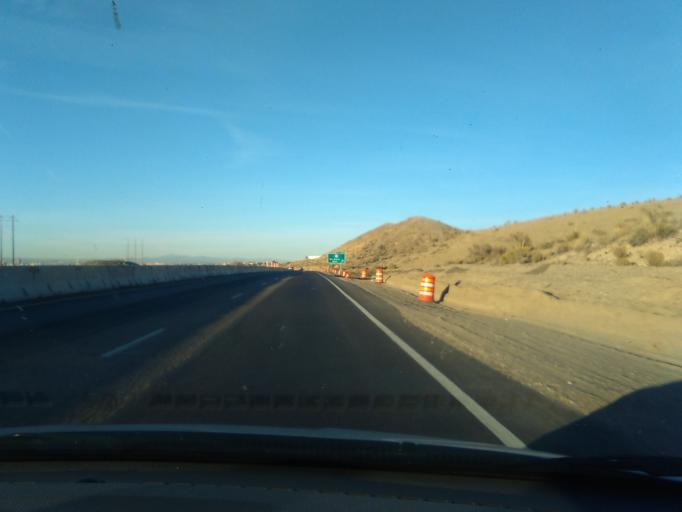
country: US
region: New Mexico
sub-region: Bernalillo County
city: South Valley
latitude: 35.0164
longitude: -106.6393
